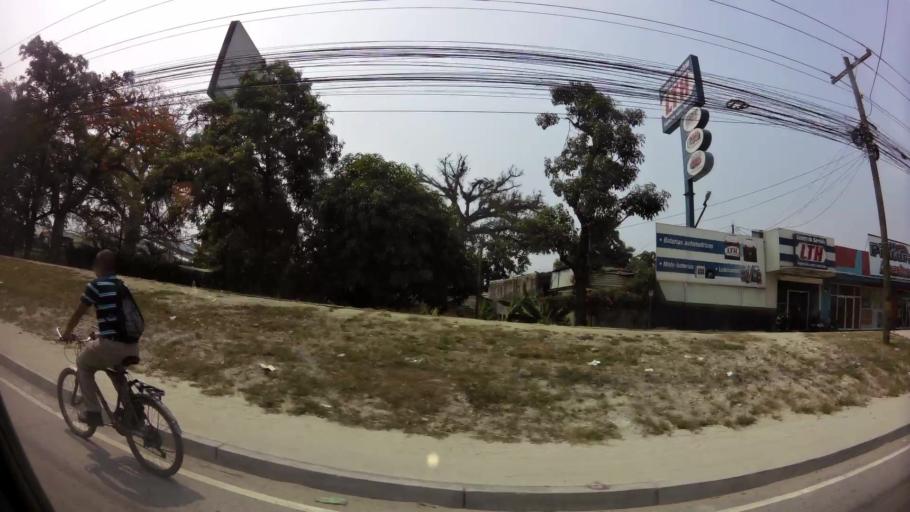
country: HN
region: Cortes
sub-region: San Pedro Sula
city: Pena Blanca
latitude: 15.5486
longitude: -88.0076
